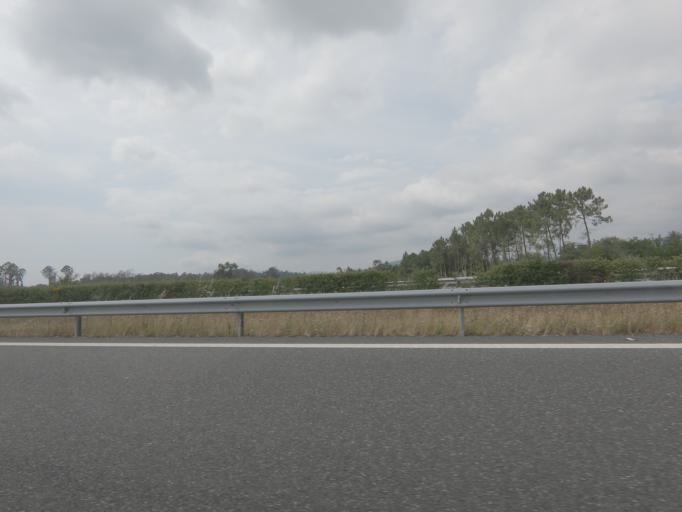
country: ES
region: Galicia
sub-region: Provincia de Pontevedra
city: Ponteareas
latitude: 42.1432
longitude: -8.4619
